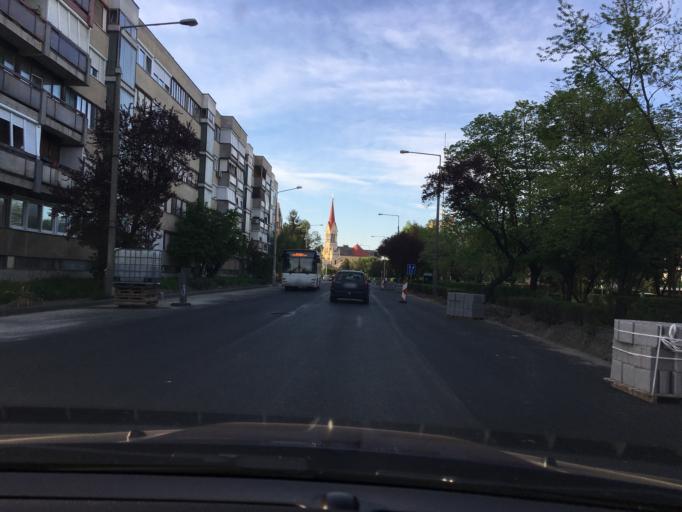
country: HU
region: Hajdu-Bihar
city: Berettyoujfalu
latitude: 47.2243
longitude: 21.5352
